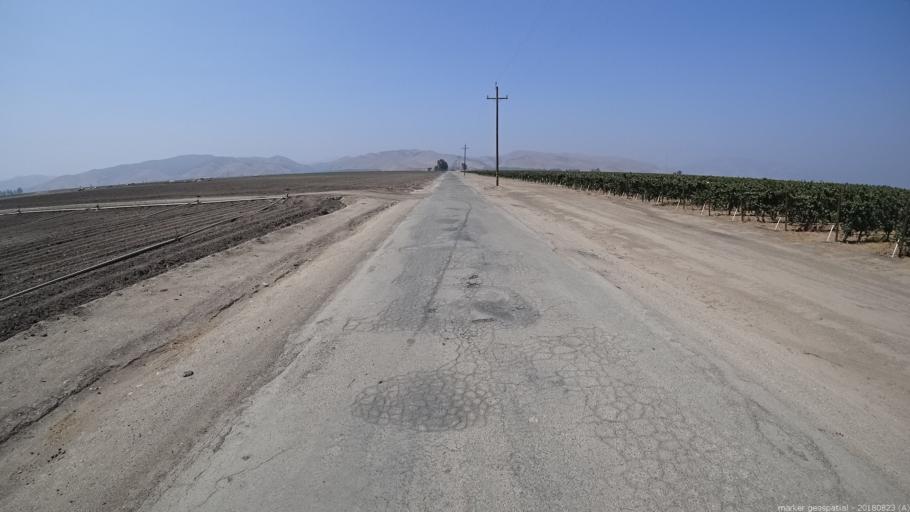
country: US
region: California
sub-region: Monterey County
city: Greenfield
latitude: 36.2833
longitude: -121.2034
